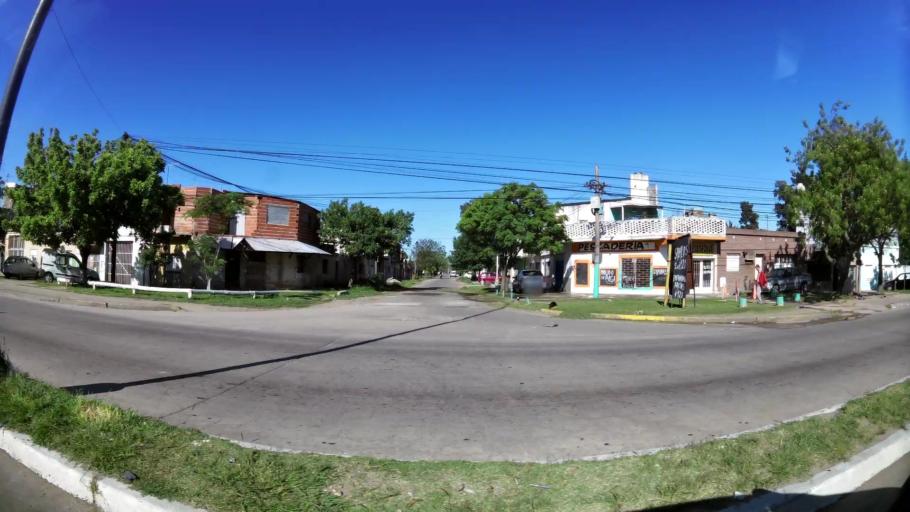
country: AR
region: Santa Fe
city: Santa Fe de la Vera Cruz
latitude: -31.6294
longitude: -60.7181
